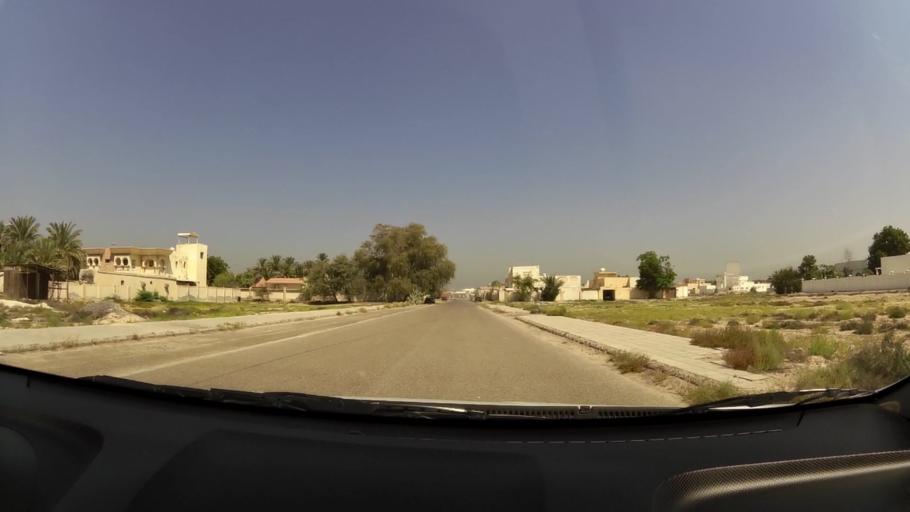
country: AE
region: Umm al Qaywayn
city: Umm al Qaywayn
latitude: 25.5547
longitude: 55.5466
